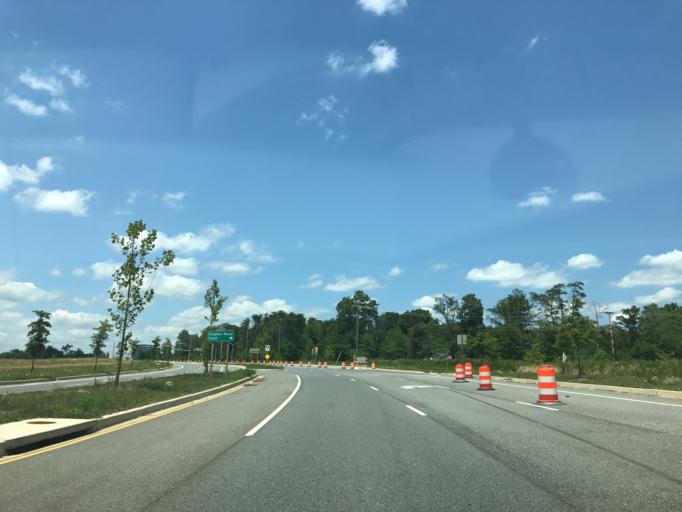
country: US
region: Maryland
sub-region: Prince George's County
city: West Laurel
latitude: 39.0765
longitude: -76.8857
